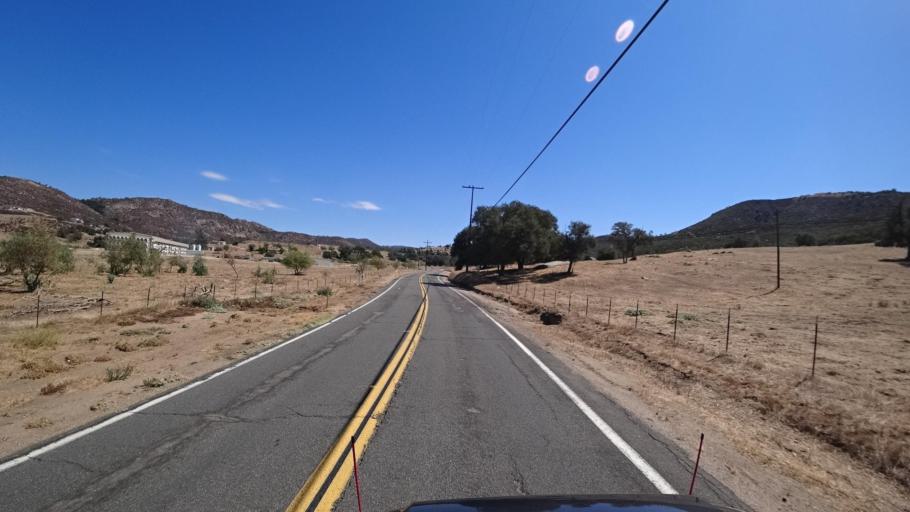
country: US
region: California
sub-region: San Diego County
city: San Diego Country Estates
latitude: 33.0494
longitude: -116.8043
